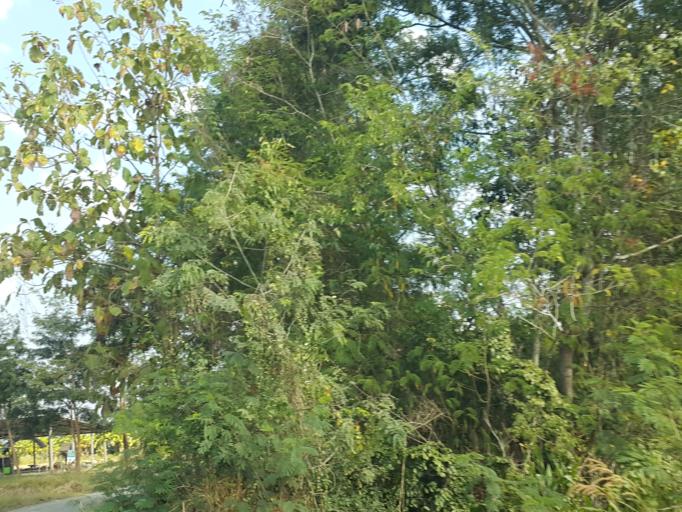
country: TH
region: Chiang Mai
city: San Sai
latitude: 18.8336
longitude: 99.1183
